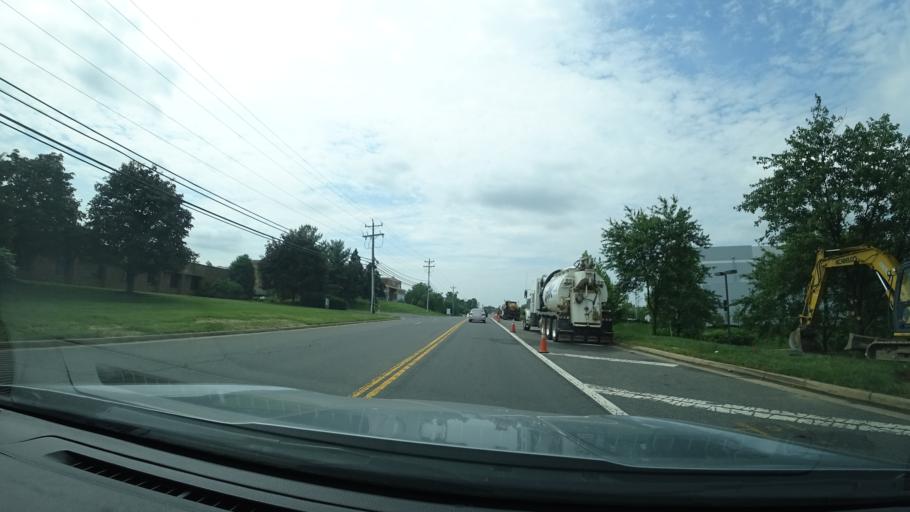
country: US
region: Virginia
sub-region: Loudoun County
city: Oak Grove
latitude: 38.9832
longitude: -77.4230
